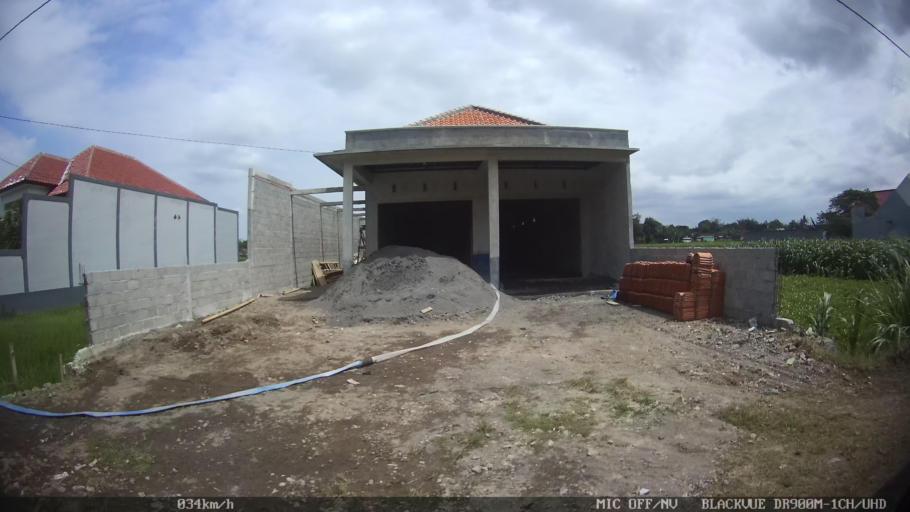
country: ID
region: Central Java
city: Candi Prambanan
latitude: -7.8128
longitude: 110.4999
